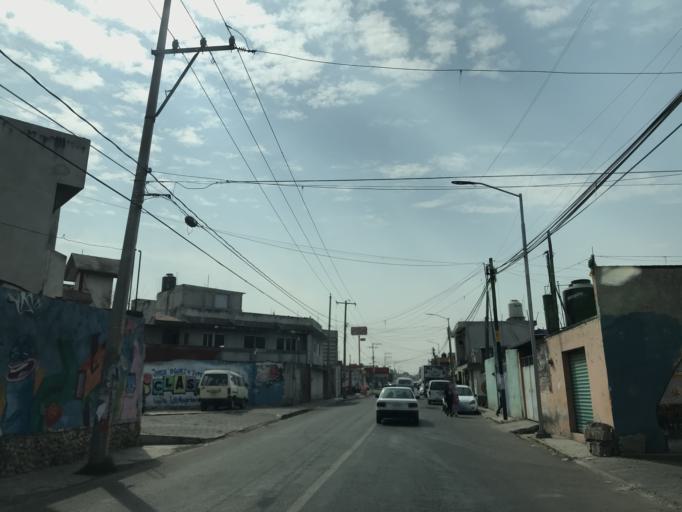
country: MX
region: Tlaxcala
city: Tenancingo
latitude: 19.1453
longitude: -98.1967
